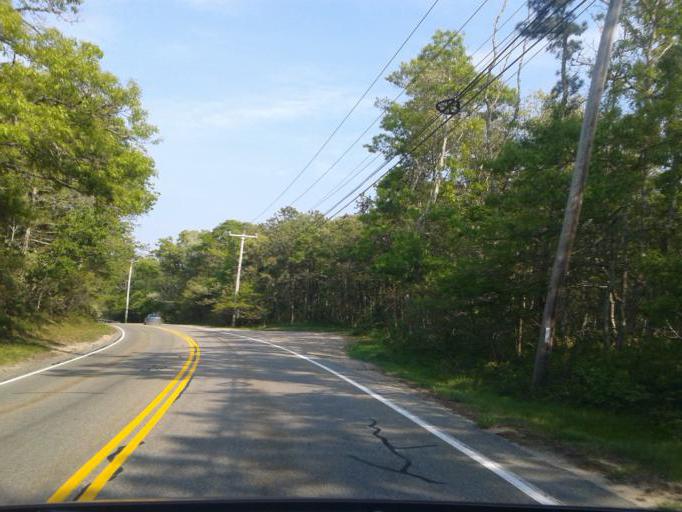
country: US
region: Massachusetts
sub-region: Barnstable County
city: West Falmouth
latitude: 41.5887
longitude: -70.6179
